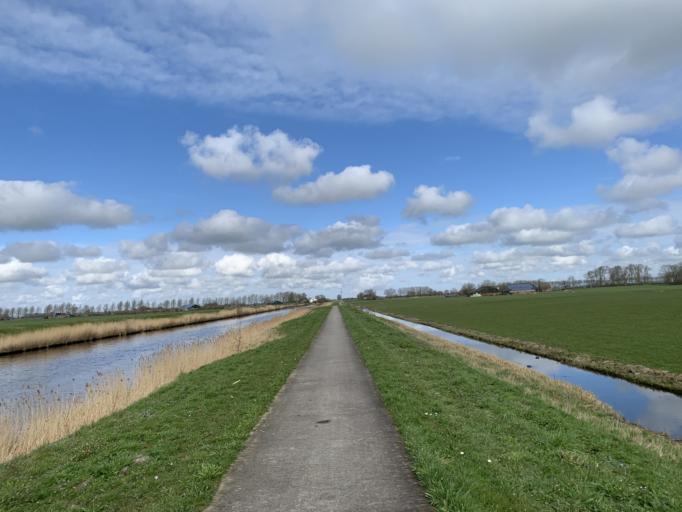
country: NL
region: Groningen
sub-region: Gemeente Zuidhorn
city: Aduard
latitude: 53.2629
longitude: 6.5078
